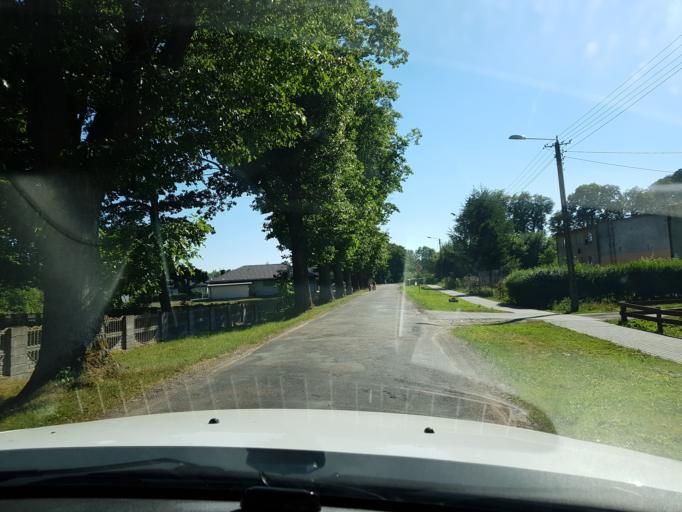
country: PL
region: West Pomeranian Voivodeship
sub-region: Powiat swidwinski
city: Slawoborze
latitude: 53.8171
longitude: 15.6778
